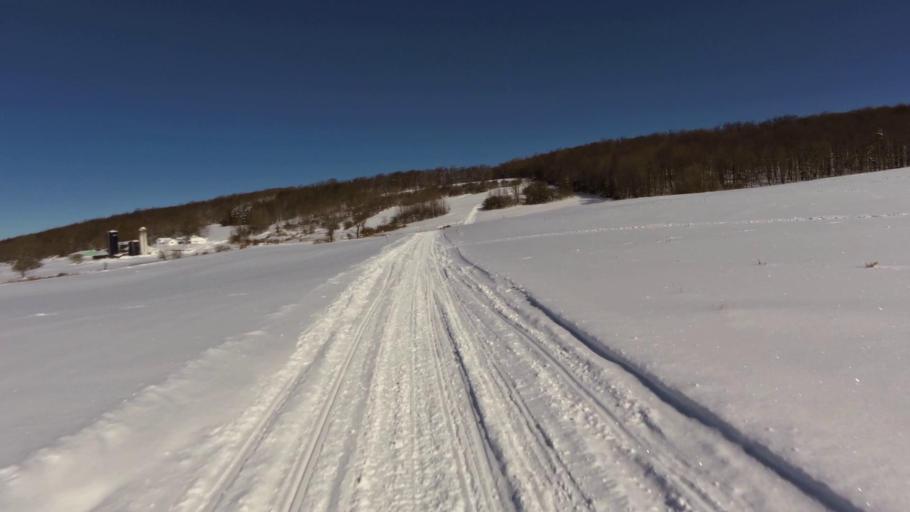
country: US
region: New York
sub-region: Chautauqua County
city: Silver Creek
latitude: 42.3754
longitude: -79.1509
